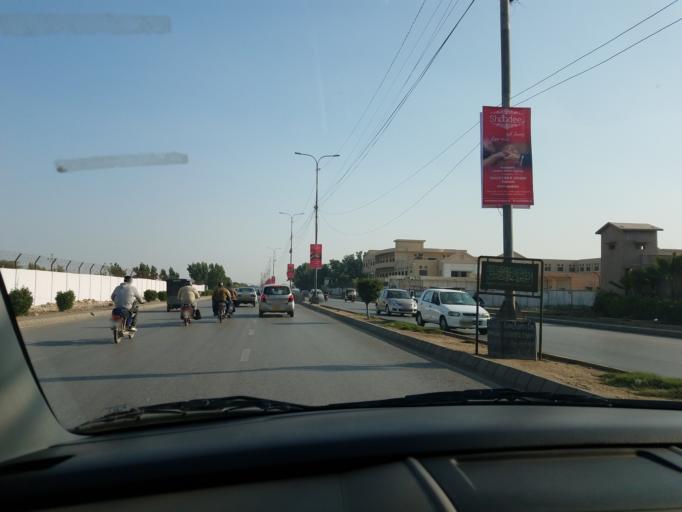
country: PK
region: Sindh
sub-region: Karachi District
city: Karachi
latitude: 24.8954
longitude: 67.1195
